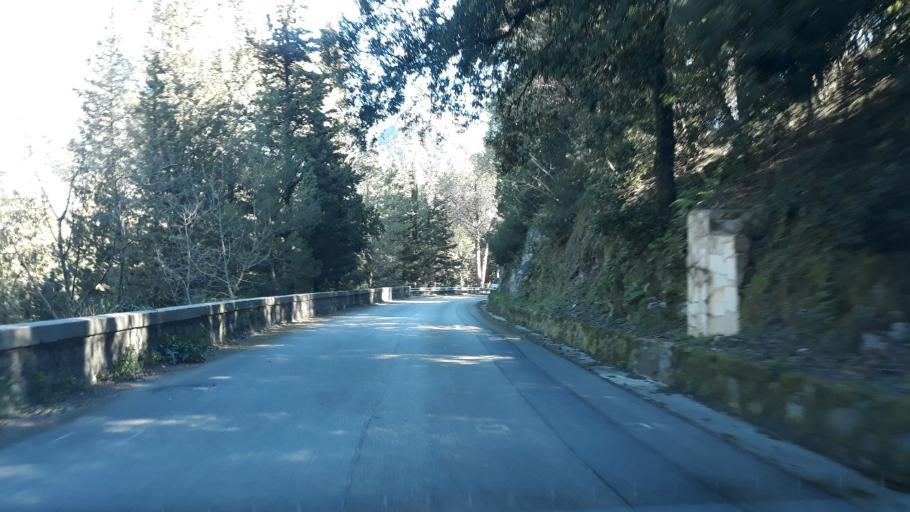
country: IT
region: Sicily
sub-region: Palermo
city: Piano dei Geli
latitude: 38.0926
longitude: 13.2545
